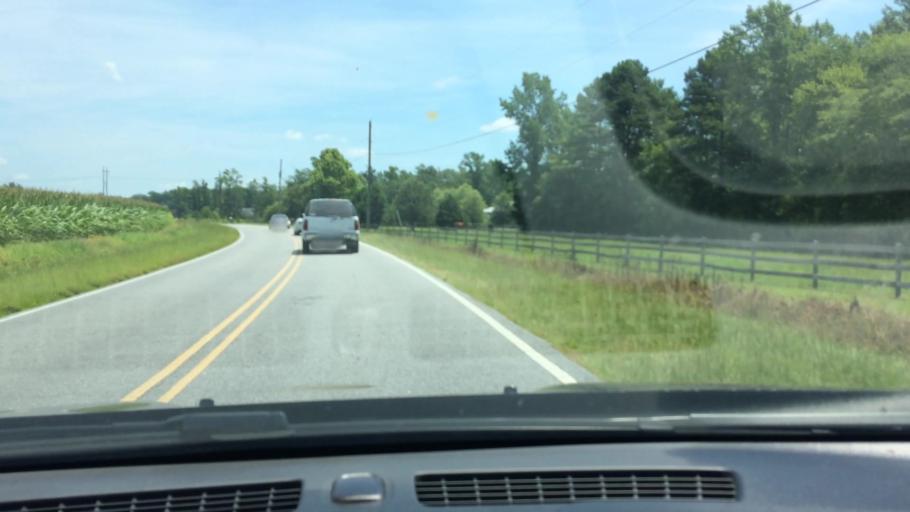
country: US
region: North Carolina
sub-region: Pitt County
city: Windsor
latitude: 35.5441
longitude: -77.2826
